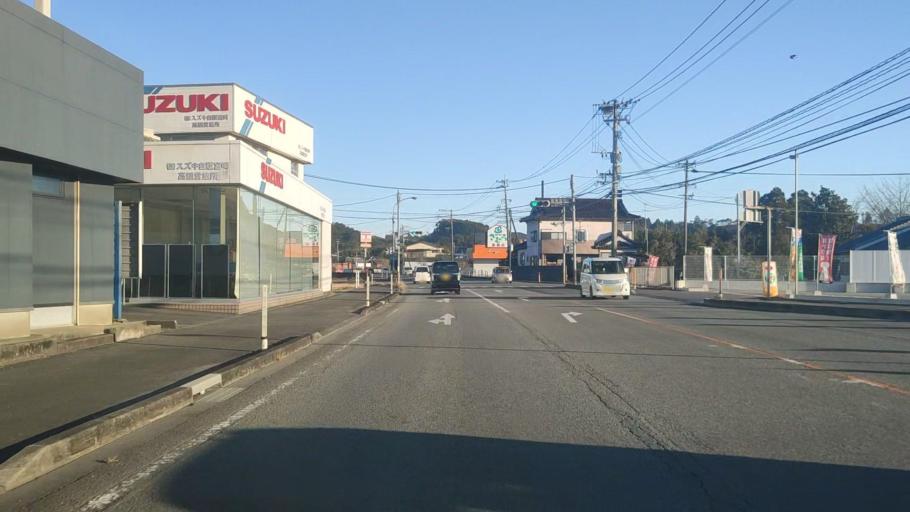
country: JP
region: Miyazaki
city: Takanabe
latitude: 32.1375
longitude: 131.5275
